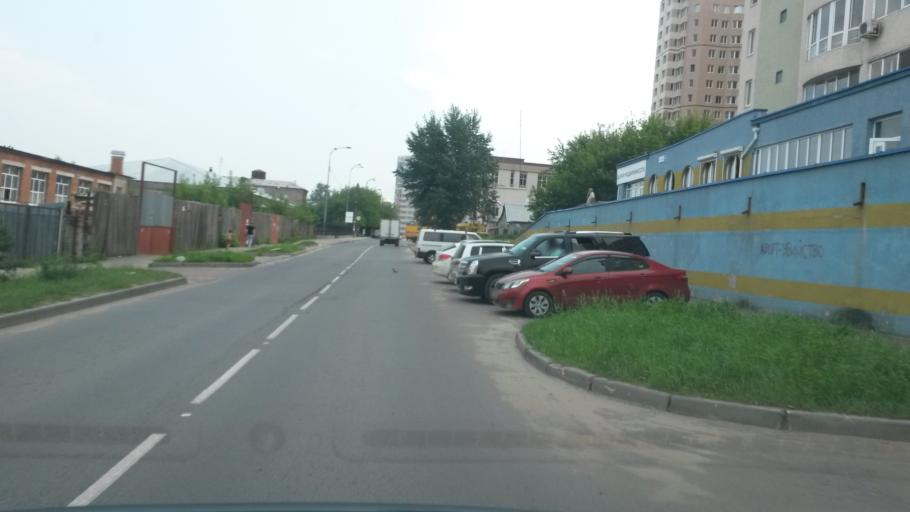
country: RU
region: Ivanovo
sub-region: Gorod Ivanovo
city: Ivanovo
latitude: 57.0024
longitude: 40.9666
